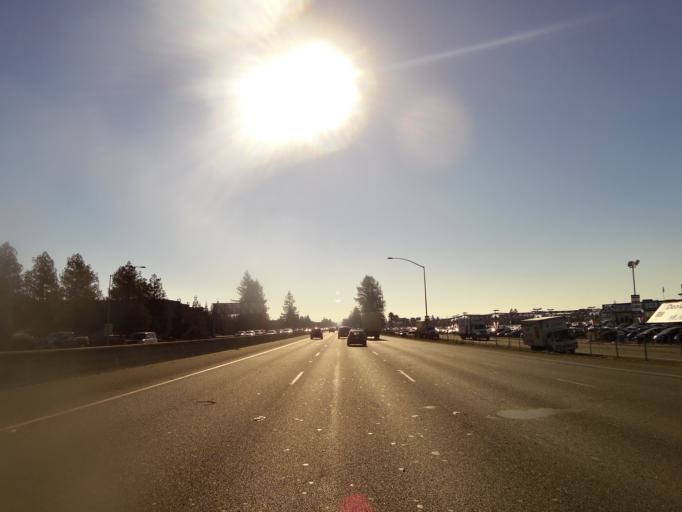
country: US
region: California
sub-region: Sonoma County
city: Roseland
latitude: 38.4119
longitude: -122.7162
